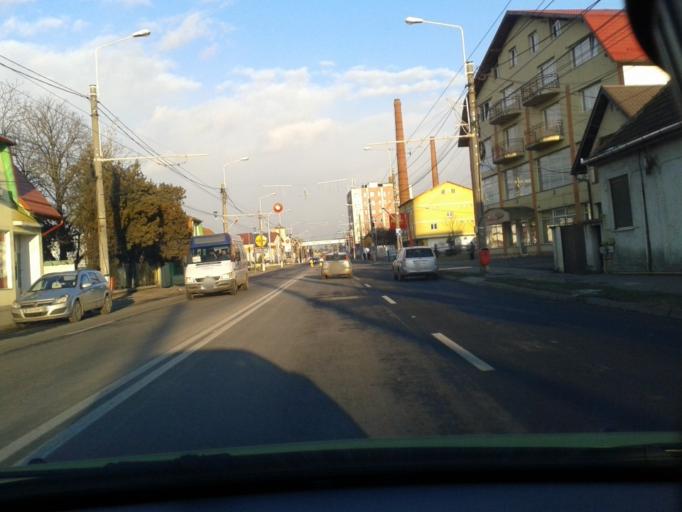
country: RO
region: Sibiu
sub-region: Municipiul Medias
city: Medias
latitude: 46.1529
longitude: 24.3349
